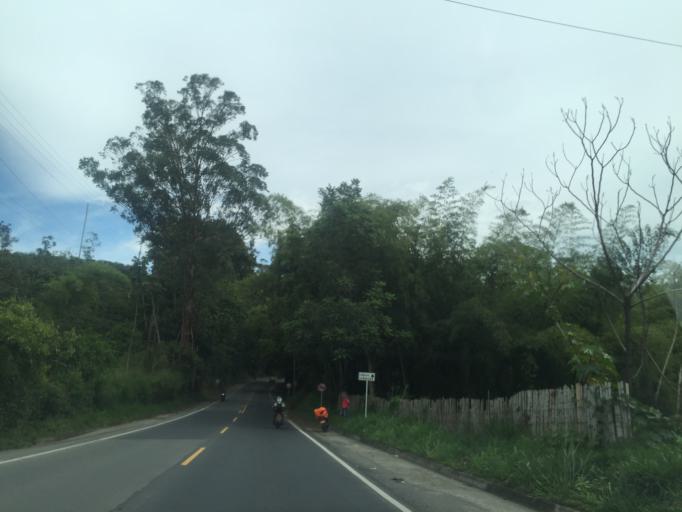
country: CO
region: Quindio
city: Montenegro
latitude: 4.5555
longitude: -75.7461
